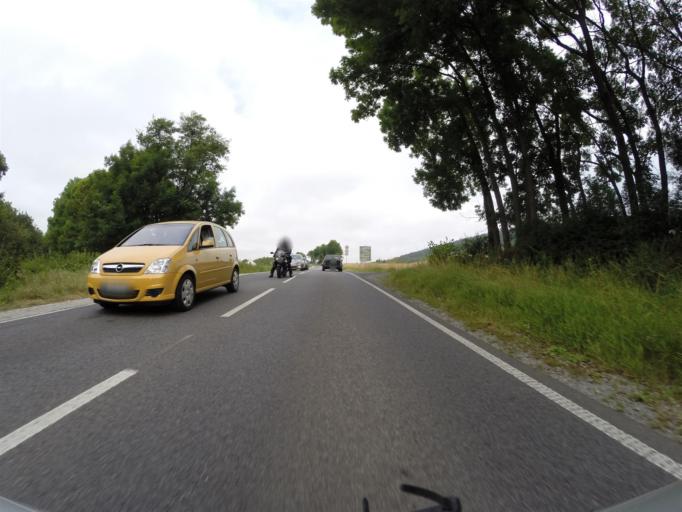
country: DE
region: Thuringia
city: Creuzburg
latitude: 51.0530
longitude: 10.2155
